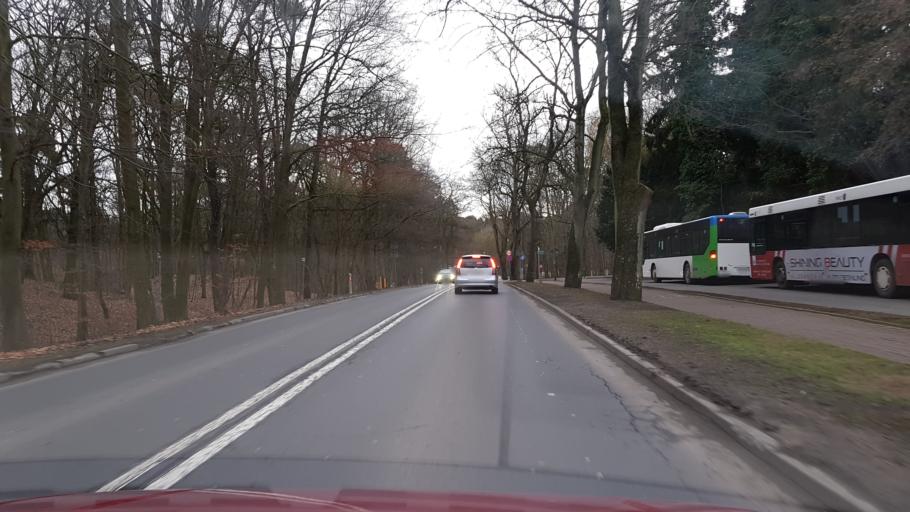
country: PL
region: West Pomeranian Voivodeship
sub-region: Szczecin
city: Szczecin
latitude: 53.4748
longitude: 14.4857
